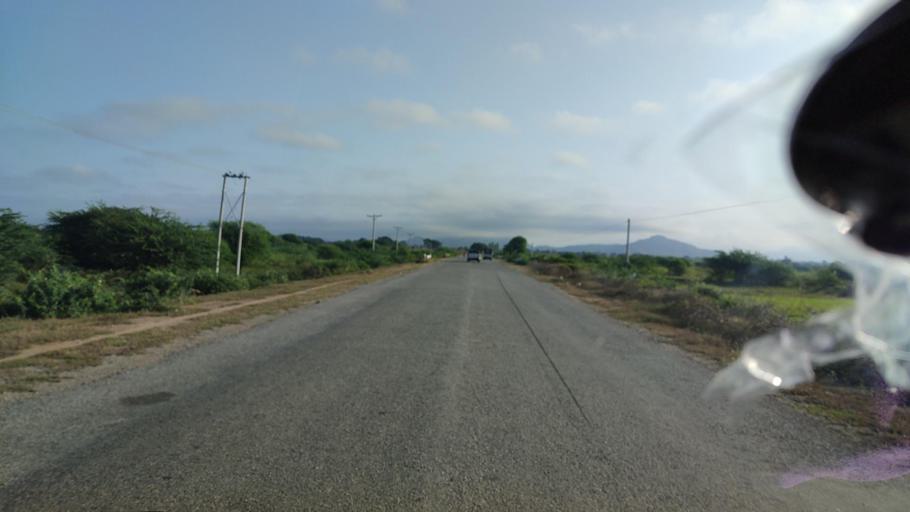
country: MM
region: Mandalay
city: Yamethin
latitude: 20.6837
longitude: 96.1525
